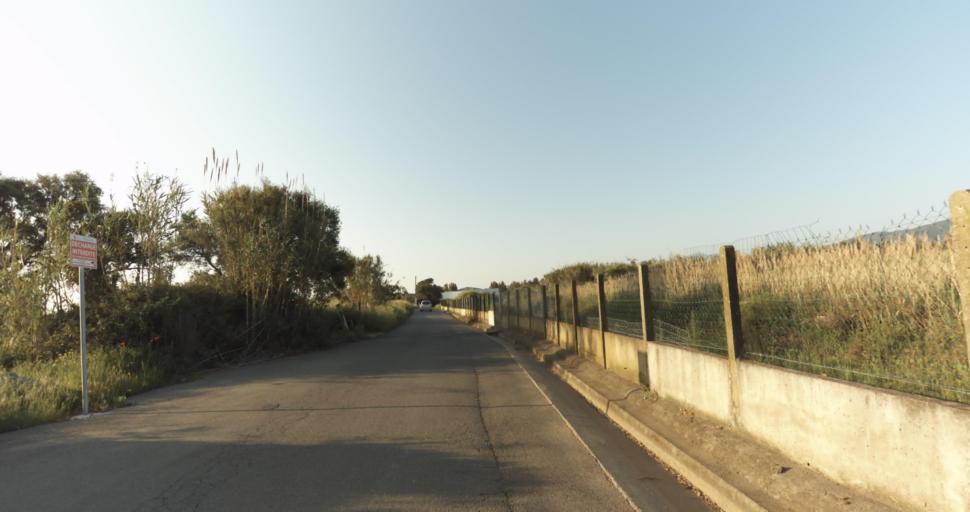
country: FR
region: Corsica
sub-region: Departement de la Haute-Corse
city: Biguglia
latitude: 42.6045
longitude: 9.4445
